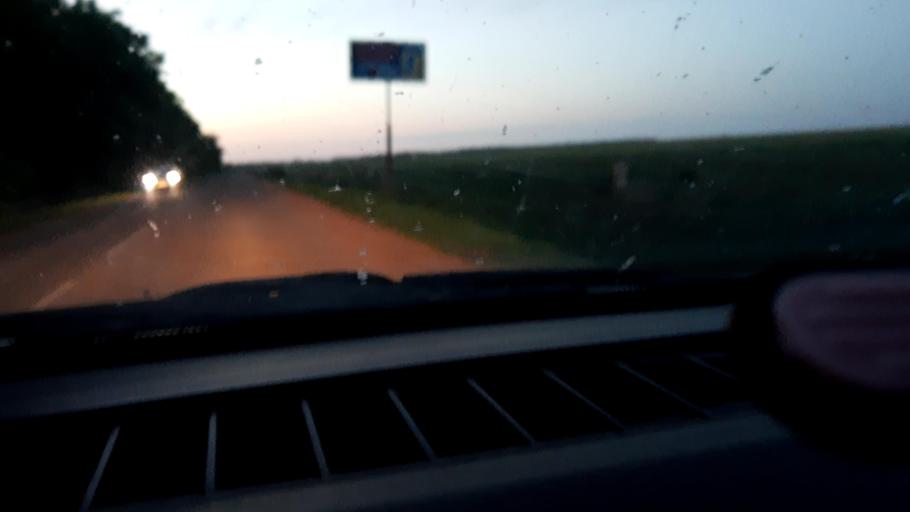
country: RU
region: Bashkortostan
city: Asanovo
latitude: 54.8168
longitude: 55.5932
